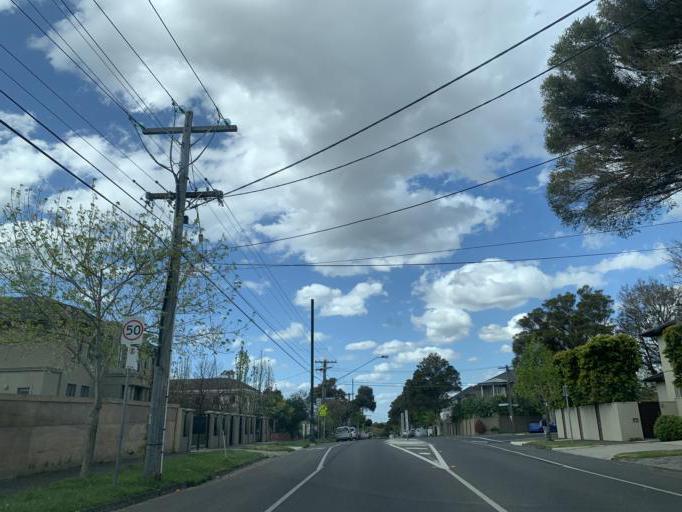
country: AU
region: Victoria
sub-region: Bayside
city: North Brighton
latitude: -37.9149
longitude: 145.0038
